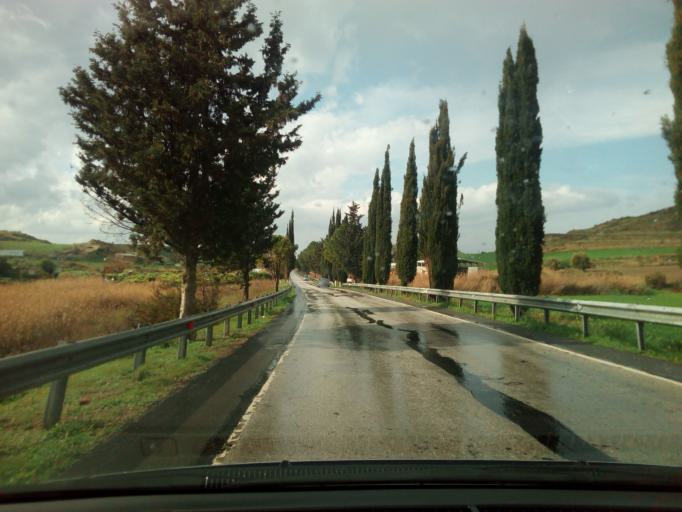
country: CY
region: Pafos
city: Polis
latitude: 35.0252
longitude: 32.4432
